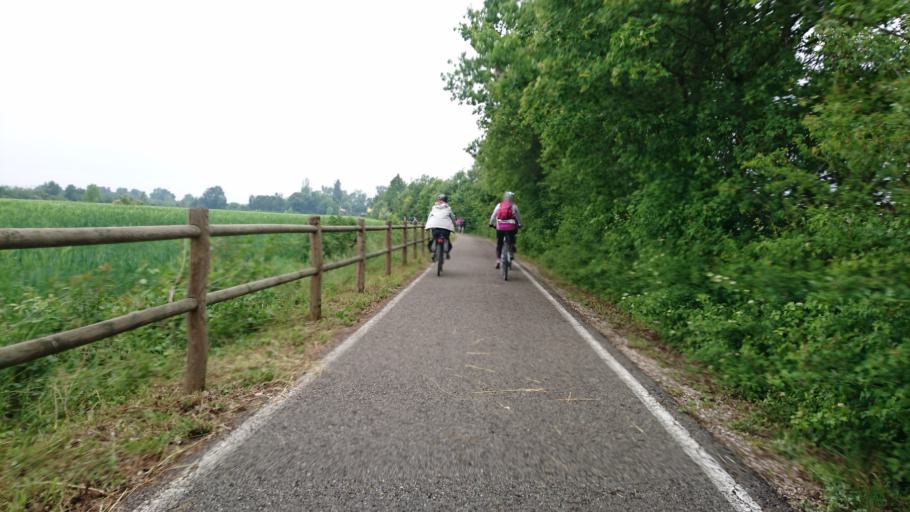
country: IT
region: Veneto
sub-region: Provincia di Padova
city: Montemerlo
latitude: 45.3834
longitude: 11.6909
